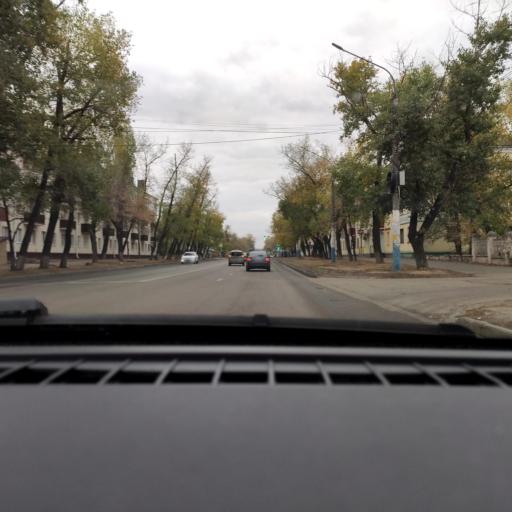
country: RU
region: Voronezj
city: Somovo
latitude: 51.7178
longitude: 39.2741
